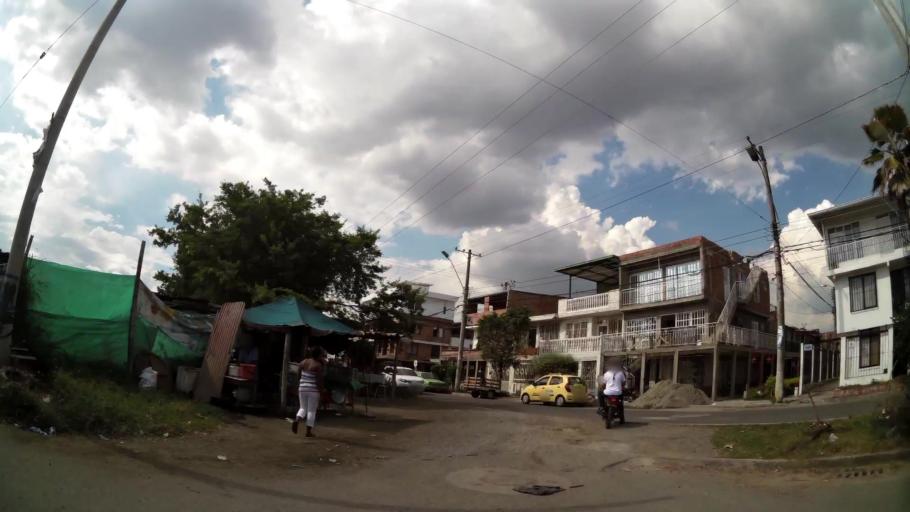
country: CO
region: Valle del Cauca
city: Cali
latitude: 3.3957
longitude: -76.5052
